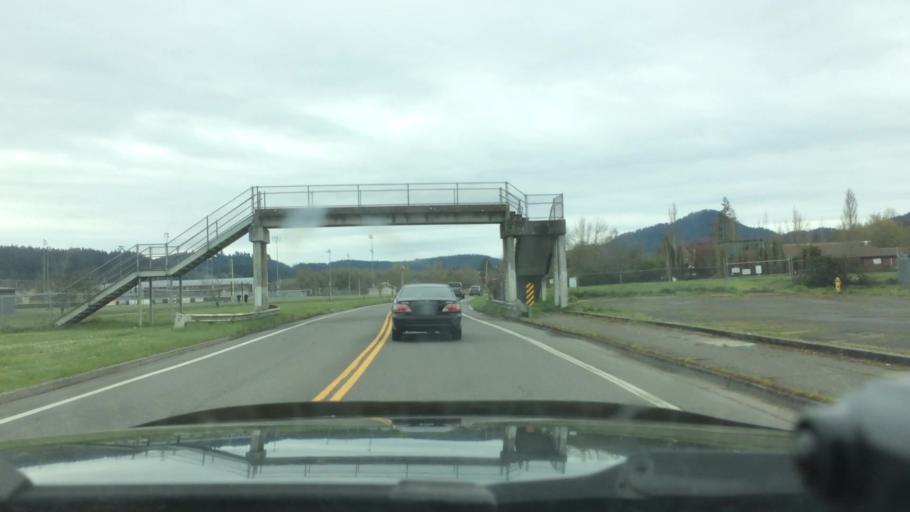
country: US
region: Oregon
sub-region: Lane County
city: Eugene
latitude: 44.0374
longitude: -123.0896
